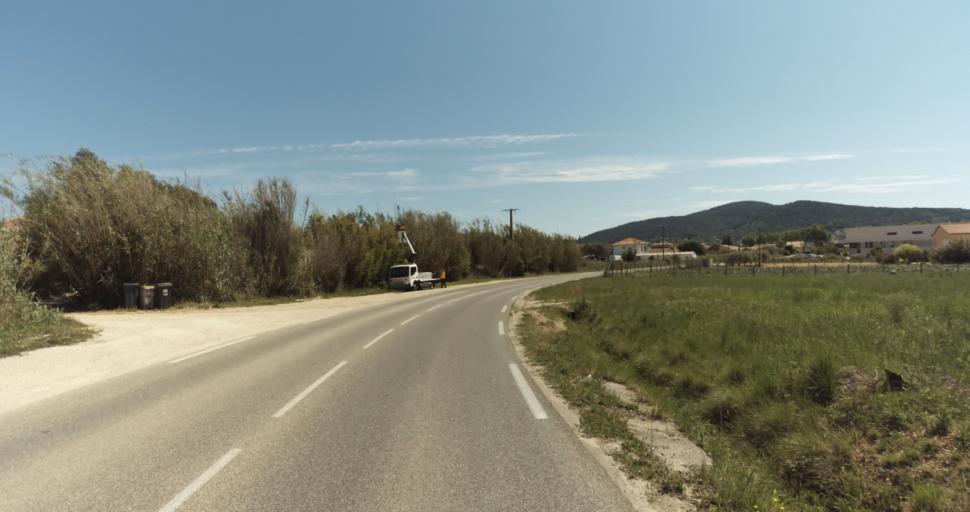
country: FR
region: Provence-Alpes-Cote d'Azur
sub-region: Departement du Var
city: La Crau
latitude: 43.1331
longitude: 6.0778
